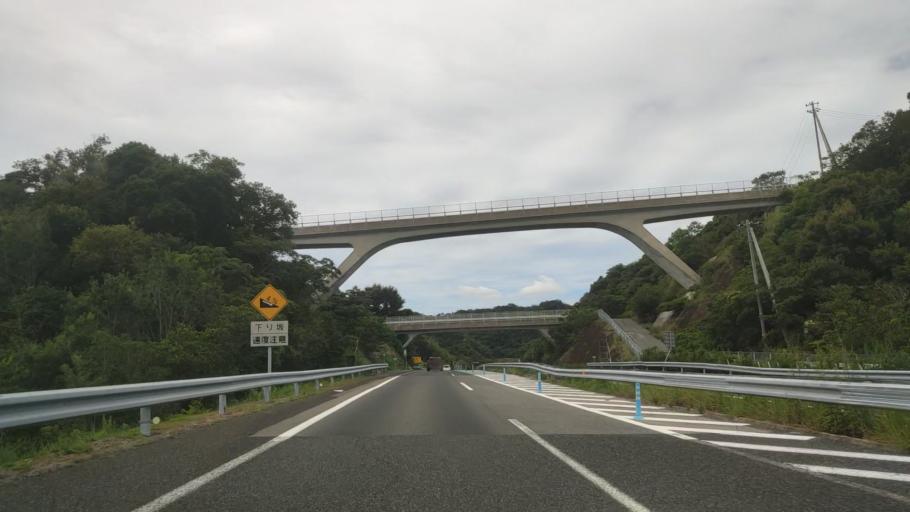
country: JP
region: Wakayama
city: Gobo
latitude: 33.8137
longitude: 135.2315
